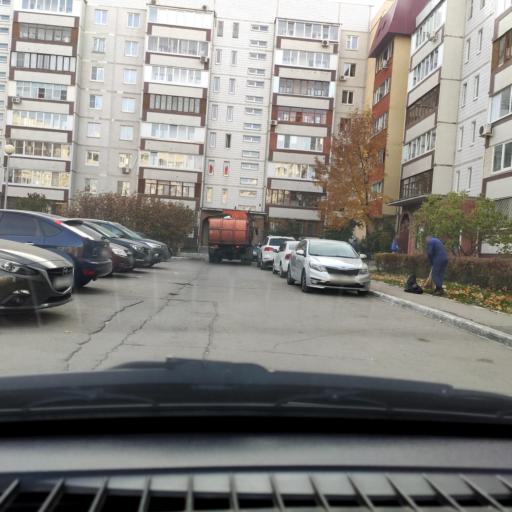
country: RU
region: Samara
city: Tol'yatti
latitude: 53.5447
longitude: 49.3690
